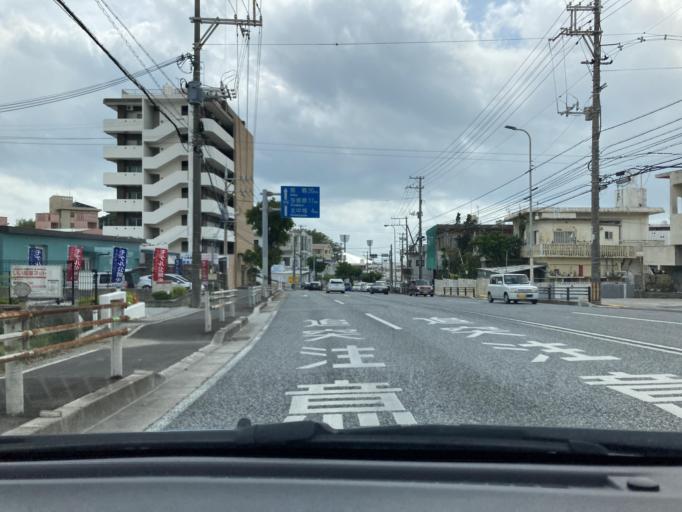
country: JP
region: Okinawa
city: Okinawa
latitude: 26.3161
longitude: 127.8188
